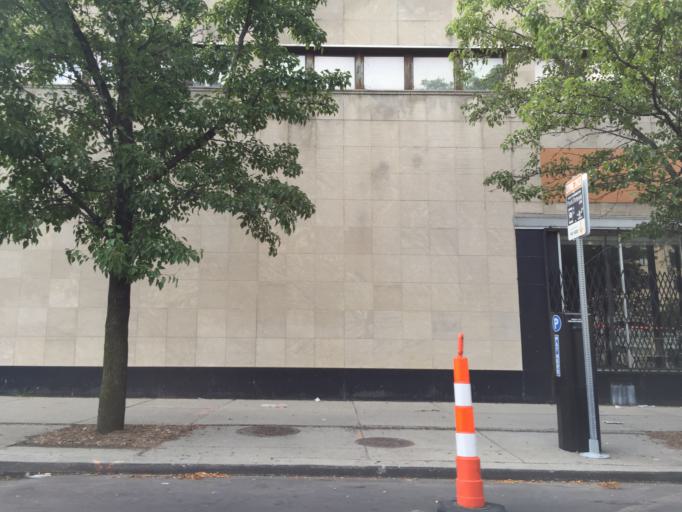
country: US
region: Michigan
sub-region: Wayne County
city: Hamtramck
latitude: 42.3700
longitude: -83.0738
